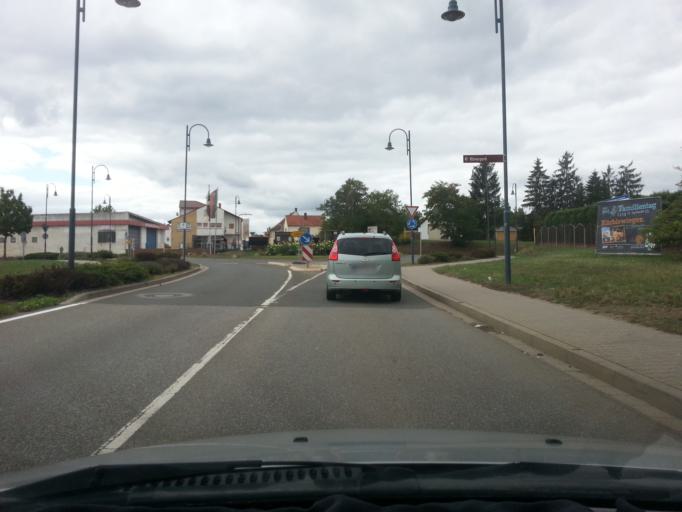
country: DE
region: Rheinland-Pfalz
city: Eisenberg
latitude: 49.5619
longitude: 8.0831
